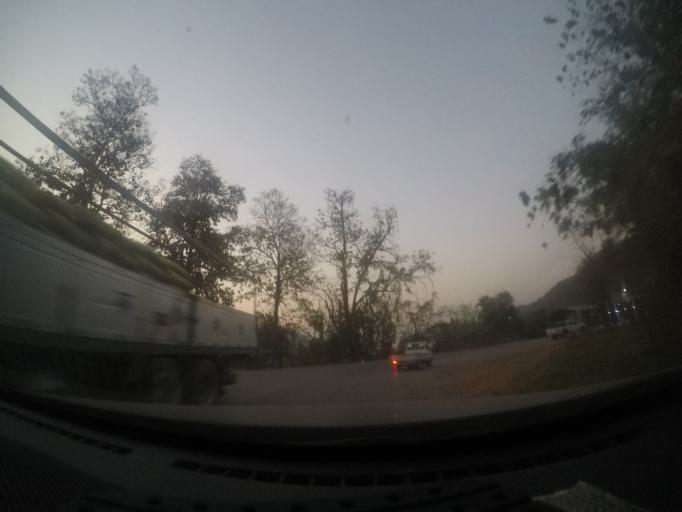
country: MM
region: Mandalay
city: Yamethin
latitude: 20.6956
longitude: 96.5050
